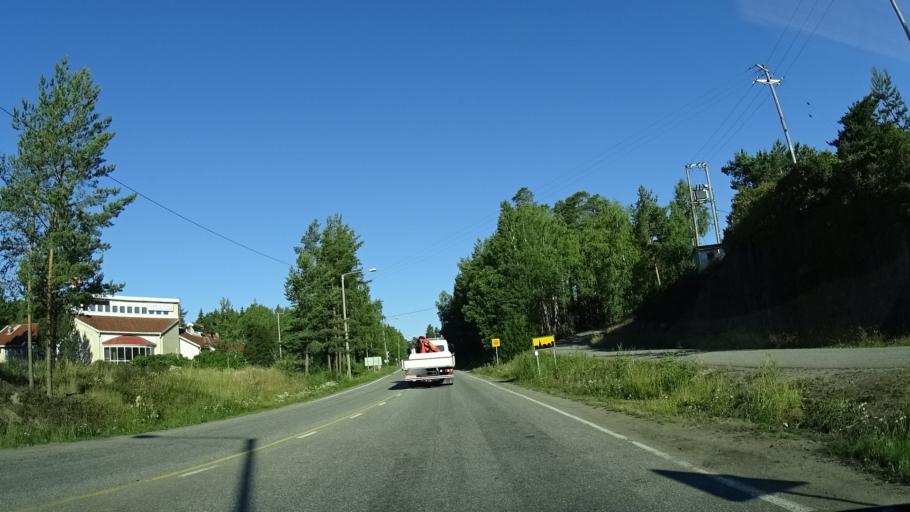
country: FI
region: Varsinais-Suomi
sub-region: Turku
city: Merimasku
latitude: 60.4589
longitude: 21.9131
